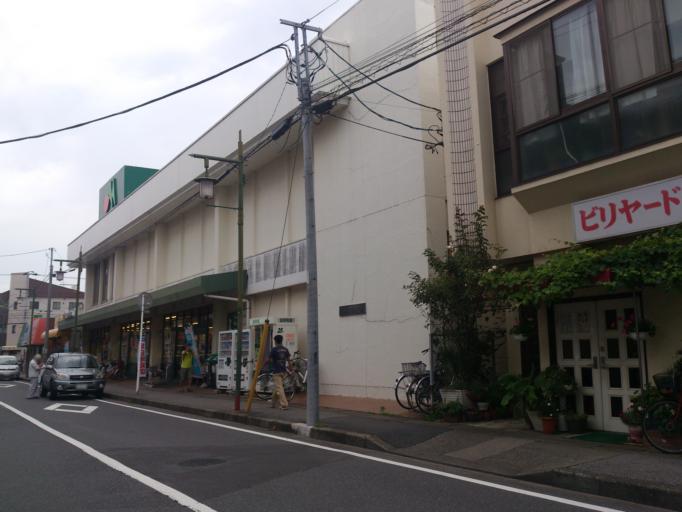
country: JP
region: Chiba
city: Matsudo
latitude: 35.7882
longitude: 139.9179
